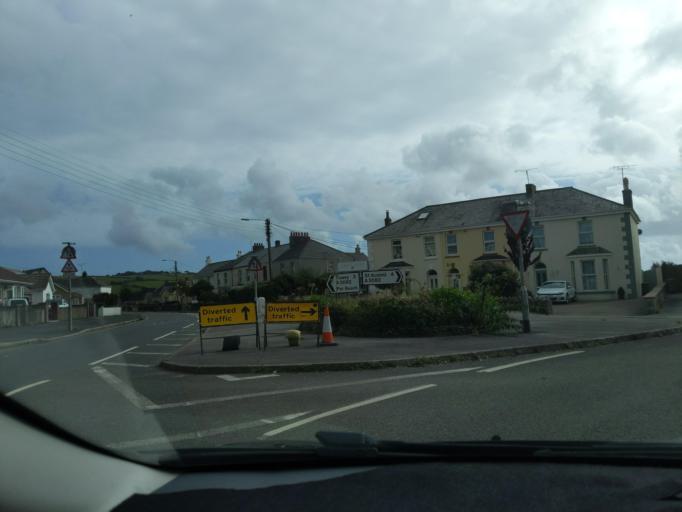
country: GB
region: England
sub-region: Cornwall
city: Par
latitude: 50.3519
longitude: -4.6994
